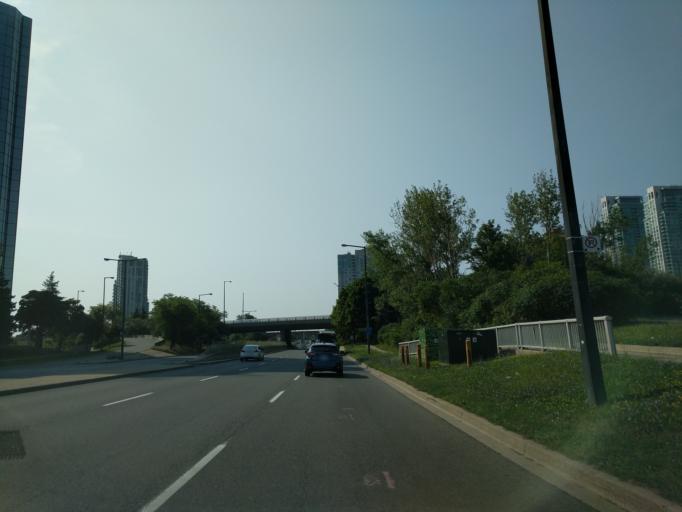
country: CA
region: Ontario
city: Scarborough
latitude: 43.7778
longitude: -79.2535
